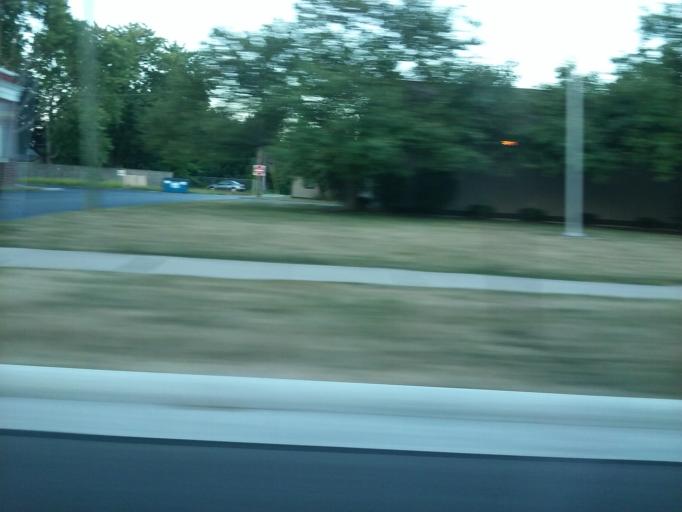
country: US
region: Ohio
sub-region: Hancock County
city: Findlay
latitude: 41.0535
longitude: -83.6500
